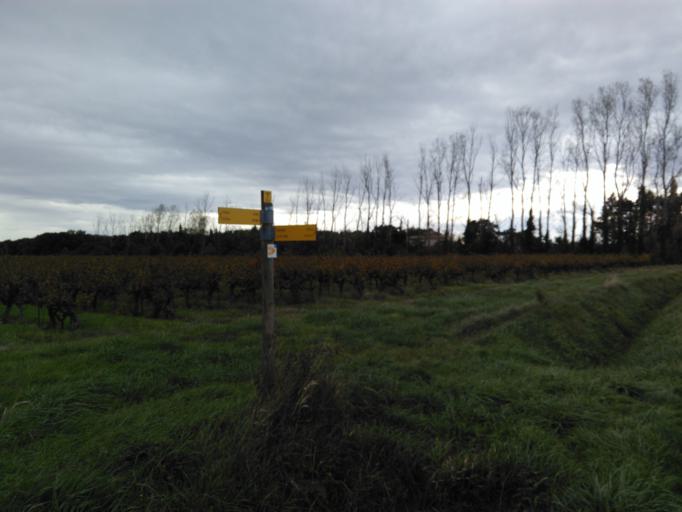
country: FR
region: Provence-Alpes-Cote d'Azur
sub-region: Departement du Vaucluse
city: Grillon
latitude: 44.3837
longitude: 4.9160
